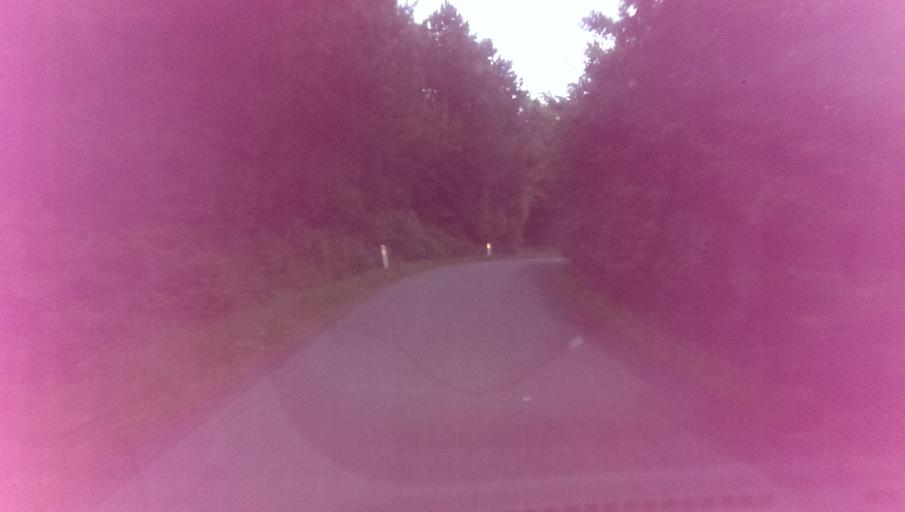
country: DK
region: South Denmark
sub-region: Esbjerg Kommune
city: Esbjerg
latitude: 55.4834
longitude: 8.5150
